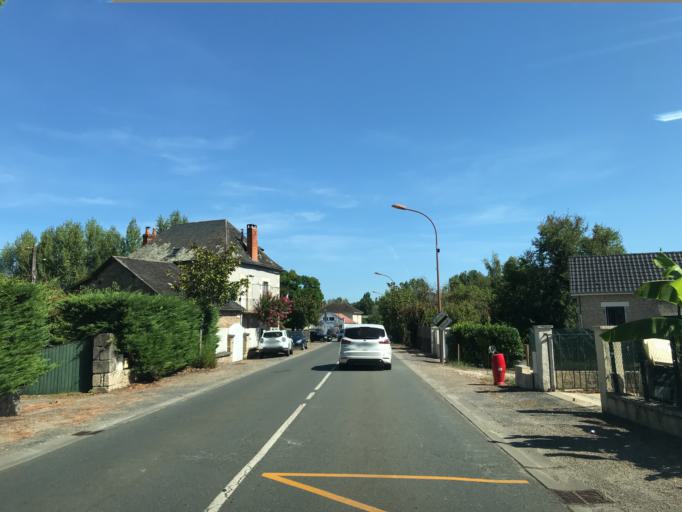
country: FR
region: Limousin
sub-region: Departement de la Correze
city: Larche
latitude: 45.1219
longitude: 1.4114
